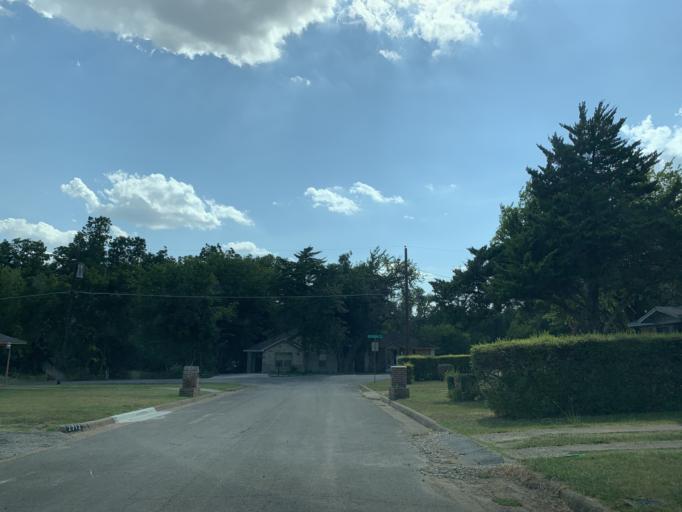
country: US
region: Texas
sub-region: Dallas County
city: Hutchins
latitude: 32.6934
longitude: -96.7772
